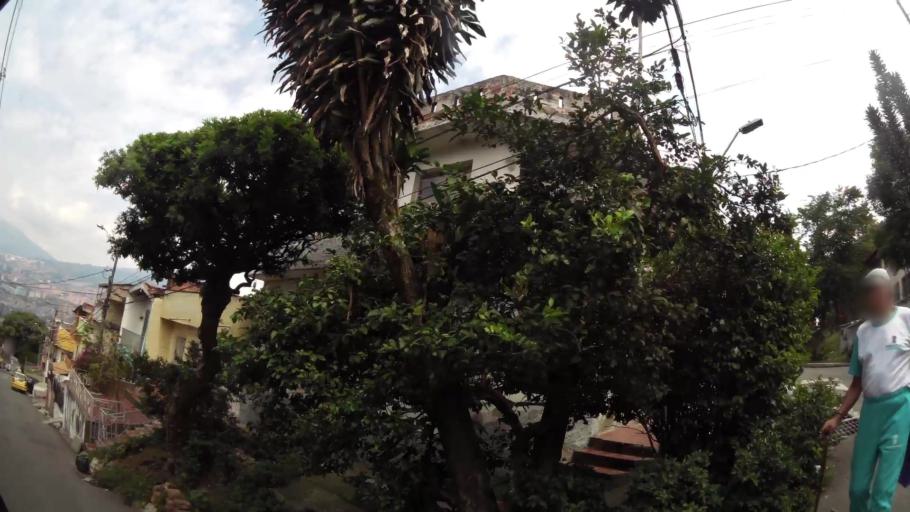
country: CO
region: Antioquia
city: Medellin
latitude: 6.2730
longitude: -75.5499
